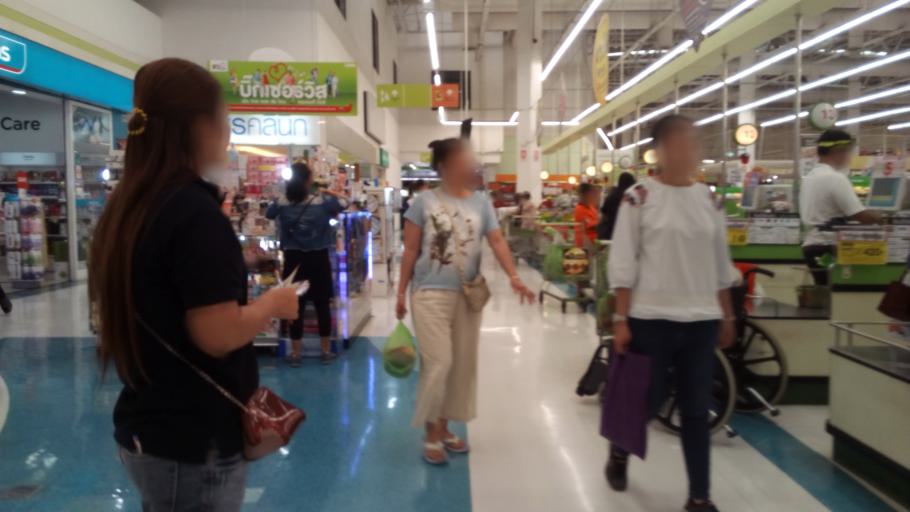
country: TH
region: Phra Nakhon Si Ayutthaya
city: Ban Bang Kadi Pathum Thani
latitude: 13.9904
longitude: 100.6182
